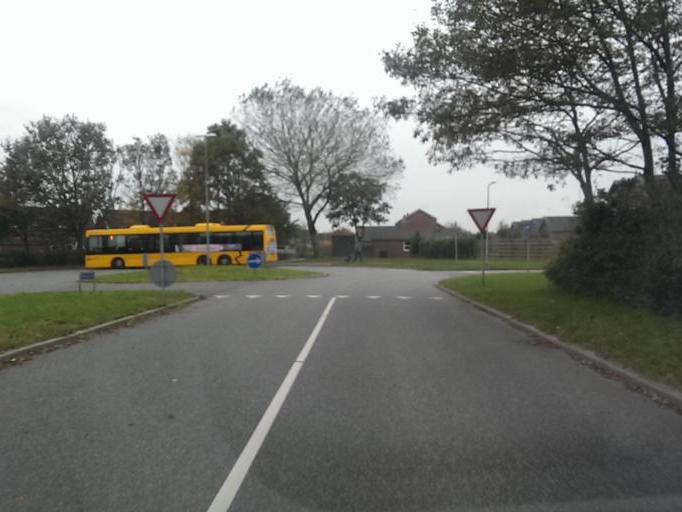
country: DK
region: South Denmark
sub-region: Esbjerg Kommune
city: Esbjerg
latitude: 55.5165
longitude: 8.4408
